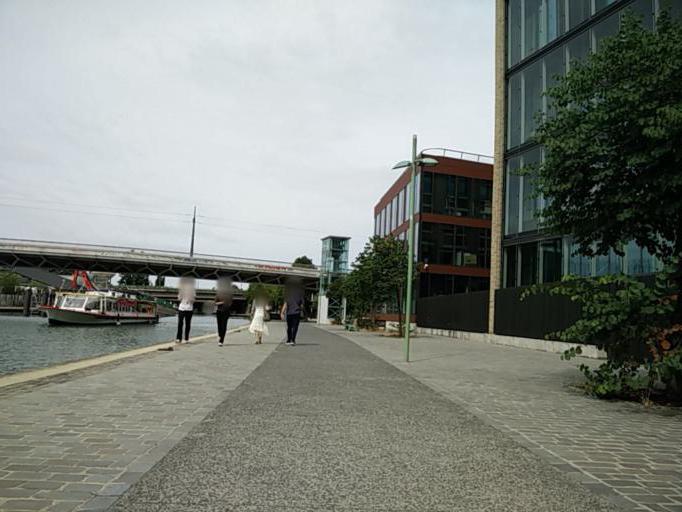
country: FR
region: Ile-de-France
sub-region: Departement de Seine-Saint-Denis
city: Pantin
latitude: 48.8963
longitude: 2.3976
